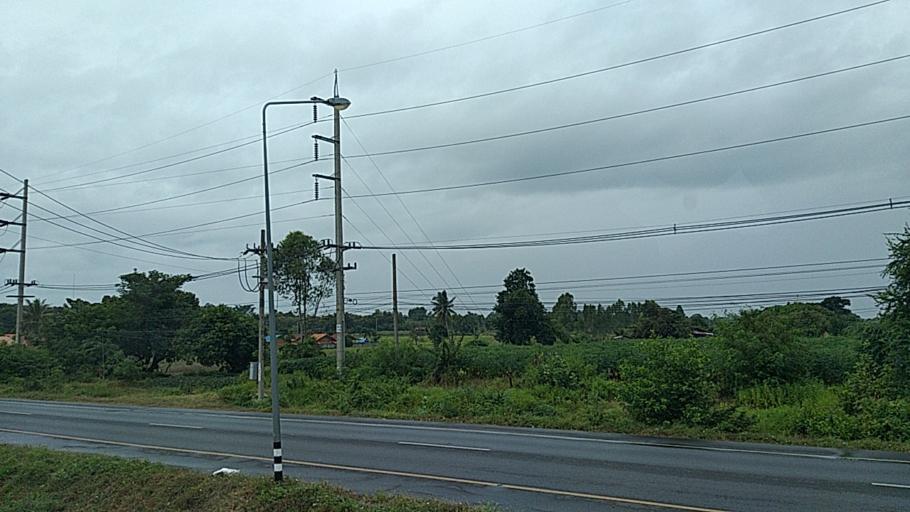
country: TH
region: Maha Sarakham
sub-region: Amphoe Borabue
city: Borabue
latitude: 16.0590
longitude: 103.1367
